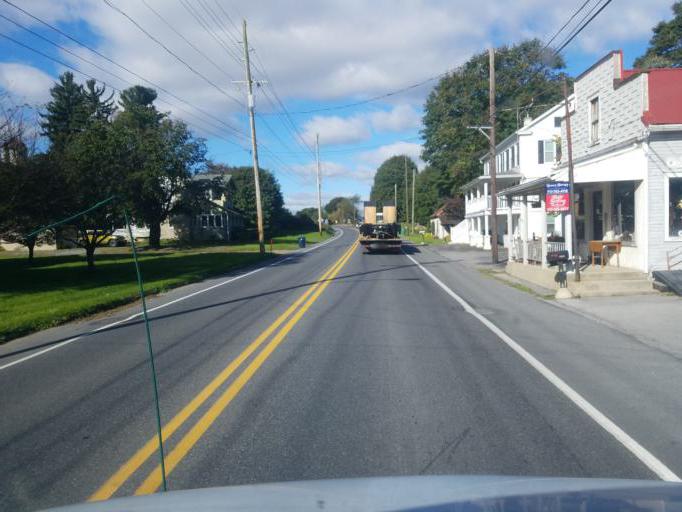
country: US
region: Pennsylvania
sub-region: Franklin County
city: Waynesboro
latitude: 39.7703
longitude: -77.6307
